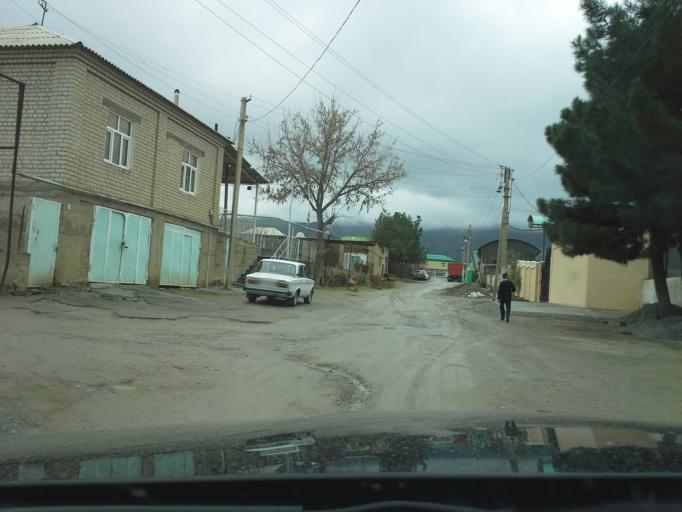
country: TM
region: Ahal
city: Abadan
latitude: 37.9606
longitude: 58.2186
